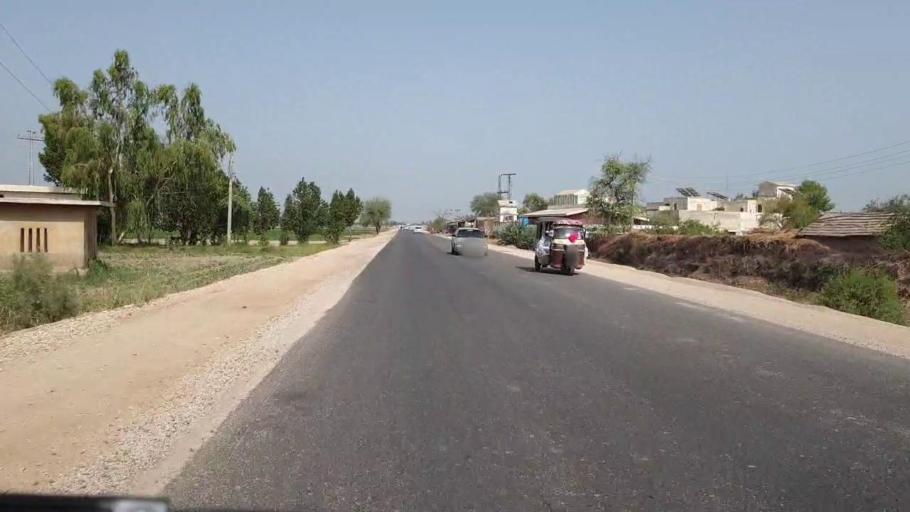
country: PK
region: Sindh
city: Sakrand
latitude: 26.2637
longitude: 68.1779
